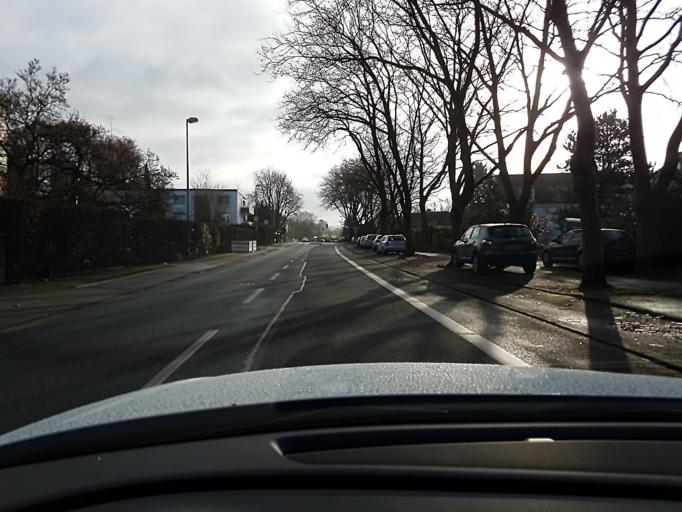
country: DE
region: North Rhine-Westphalia
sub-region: Regierungsbezirk Dusseldorf
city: Muelheim (Ruhr)
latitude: 51.4056
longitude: 6.8972
